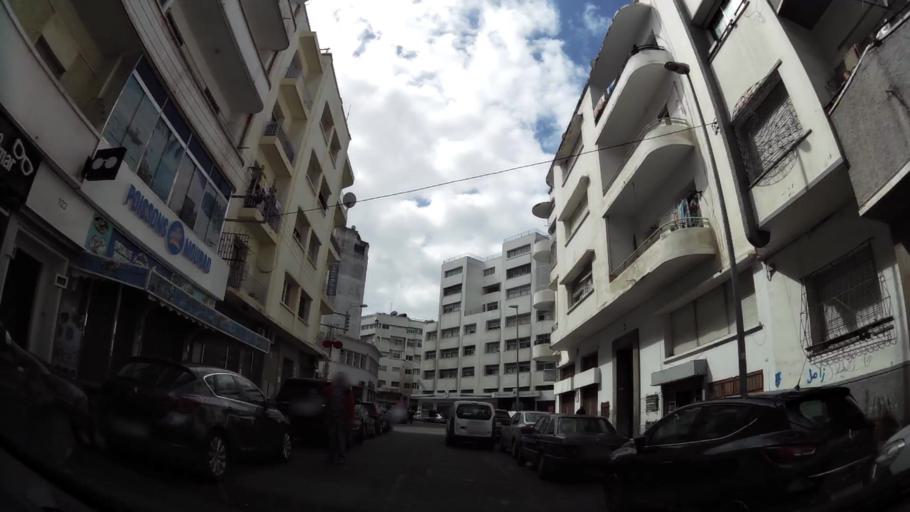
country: MA
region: Grand Casablanca
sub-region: Casablanca
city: Casablanca
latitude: 33.5916
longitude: -7.6055
